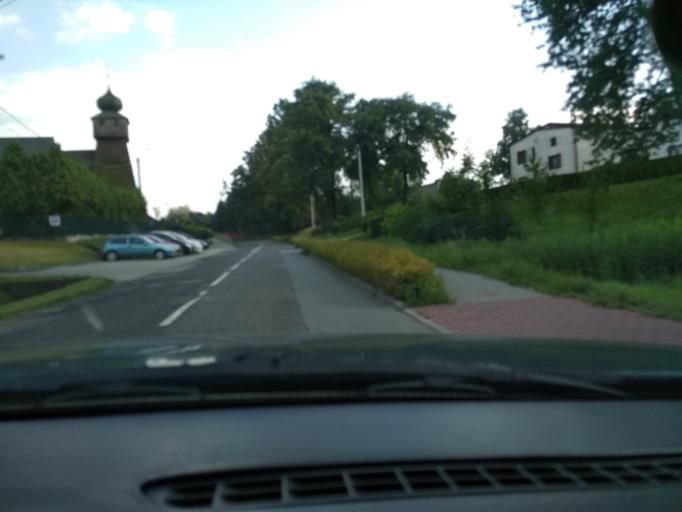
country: PL
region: Silesian Voivodeship
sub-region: Powiat cieszynski
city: Strumien
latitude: 49.9354
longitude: 18.7969
